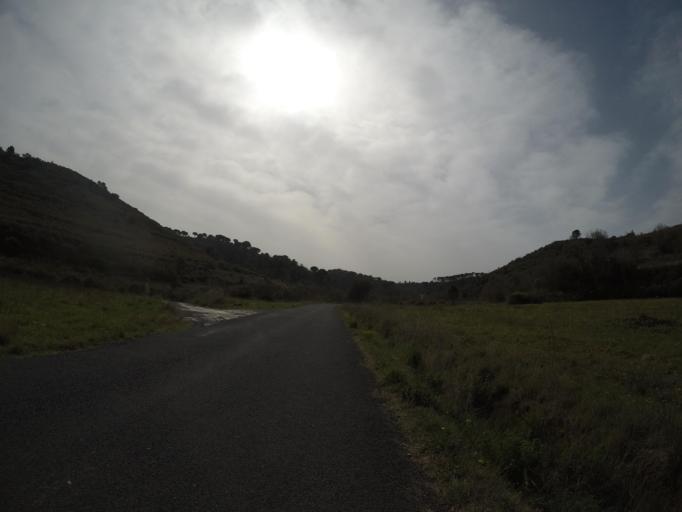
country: FR
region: Languedoc-Roussillon
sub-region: Departement des Pyrenees-Orientales
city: Estagel
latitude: 42.7629
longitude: 2.7072
